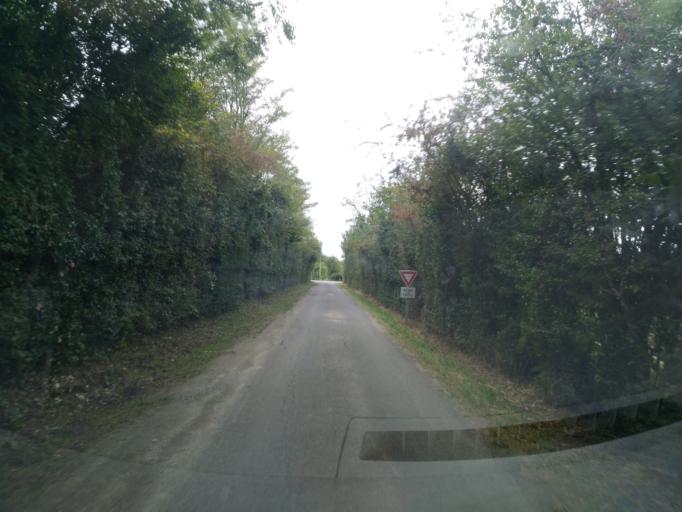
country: FR
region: Poitou-Charentes
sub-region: Departement de la Charente-Maritime
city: Pons
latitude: 45.5695
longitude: -0.5396
